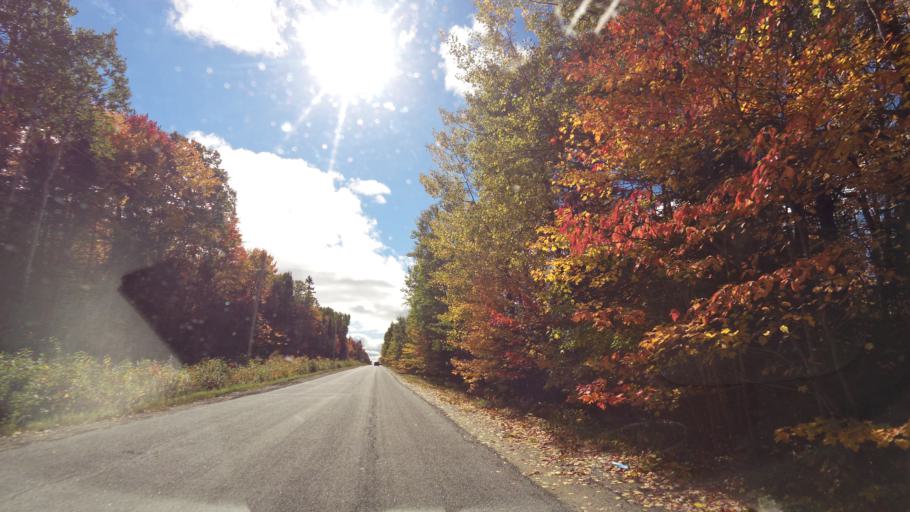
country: CA
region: Ontario
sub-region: Nipissing District
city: North Bay
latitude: 46.3577
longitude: -79.4872
